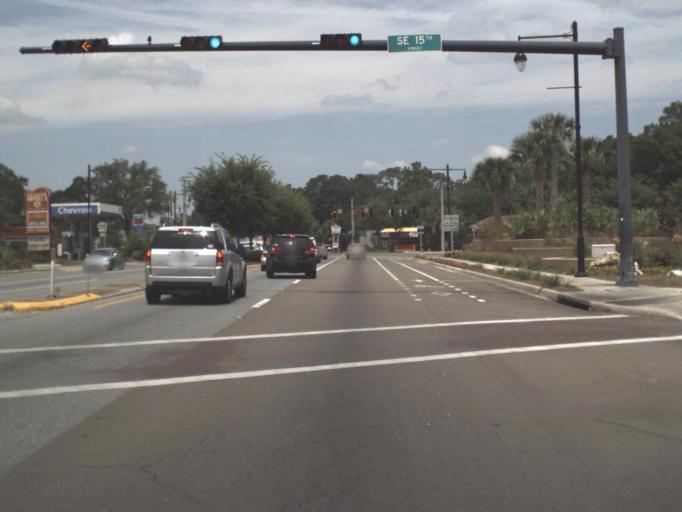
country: US
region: Florida
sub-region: Alachua County
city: Gainesville
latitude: 29.6513
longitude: -82.3059
